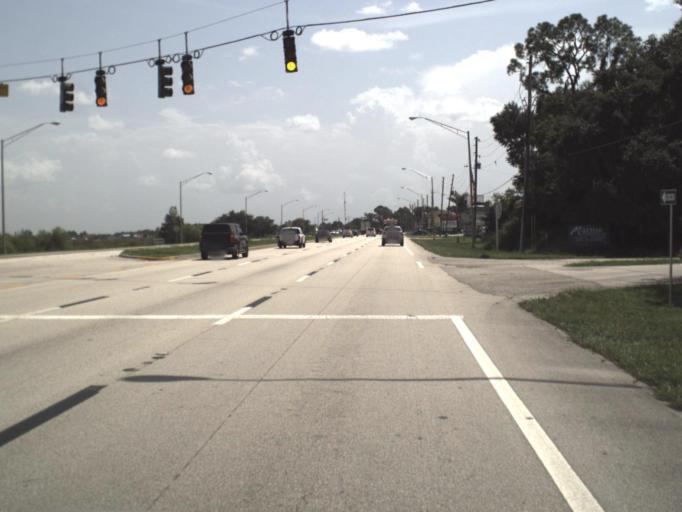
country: US
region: Florida
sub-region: Highlands County
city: Sebring
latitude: 27.4742
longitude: -81.4700
